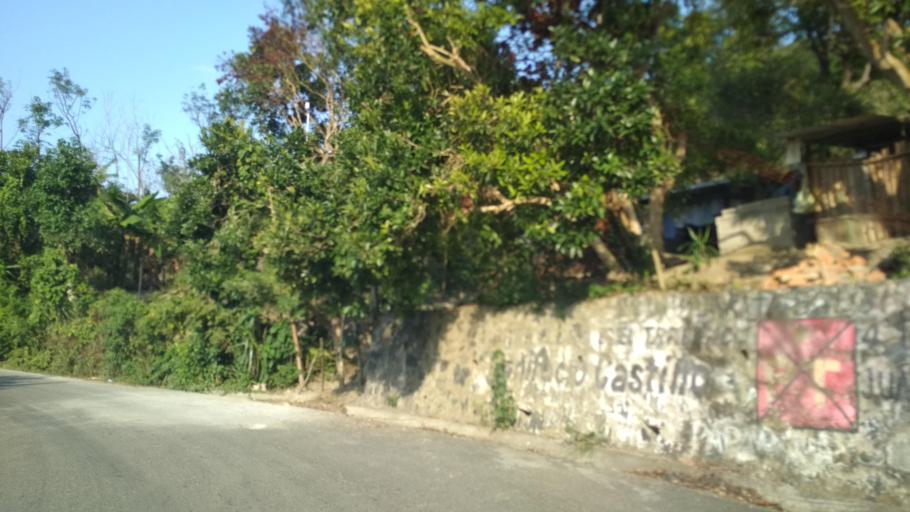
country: MX
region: Veracruz
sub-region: Poza Rica de Hidalgo
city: Arroyo del Maiz Uno
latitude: 20.4876
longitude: -97.3842
